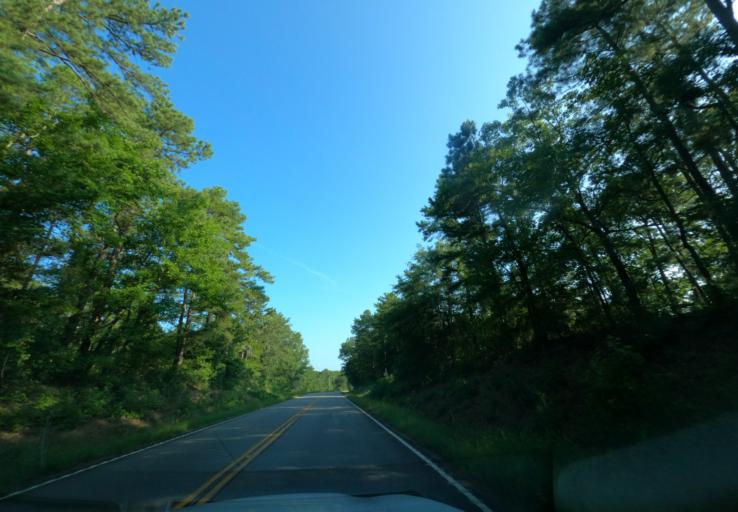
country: US
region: South Carolina
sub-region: Edgefield County
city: Murphys Estates
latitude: 33.5869
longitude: -81.9787
